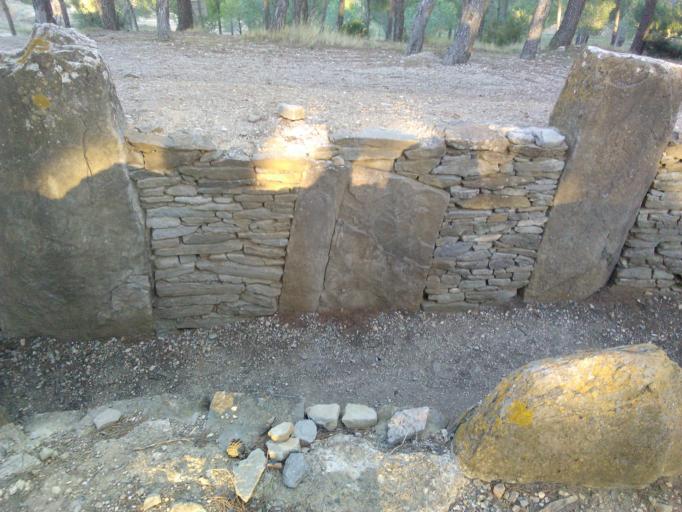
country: FR
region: Languedoc-Roussillon
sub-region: Departement de l'Aude
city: Pepieux
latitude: 43.3127
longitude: 2.6799
